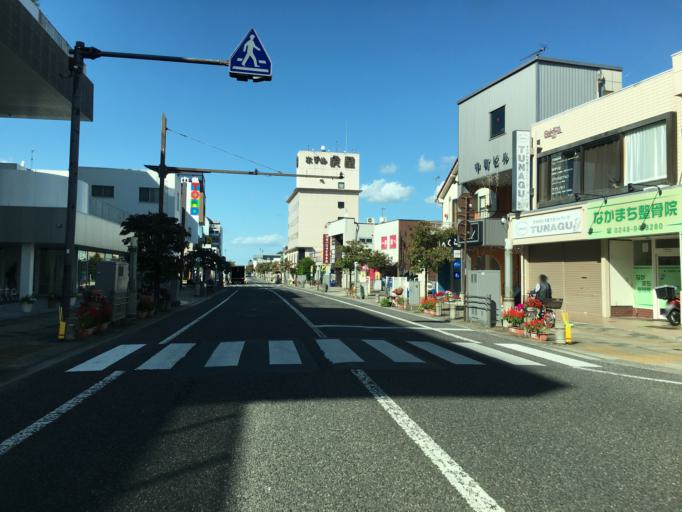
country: JP
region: Fukushima
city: Sukagawa
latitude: 37.2886
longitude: 140.3757
